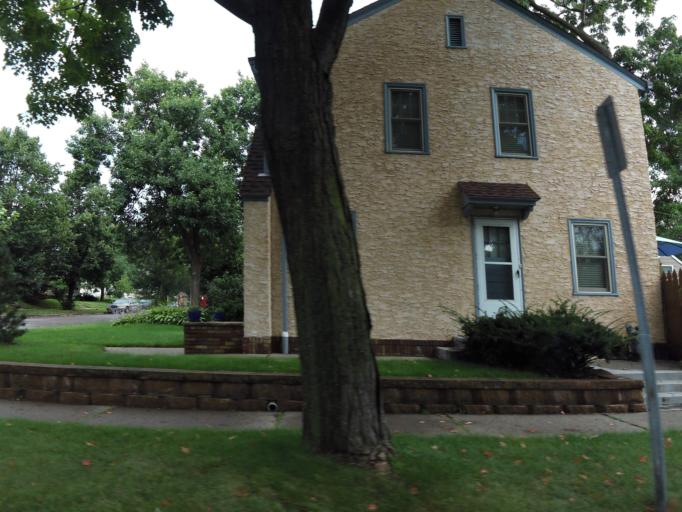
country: US
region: Minnesota
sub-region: Dakota County
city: Mendota Heights
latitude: 44.9307
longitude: -93.1654
